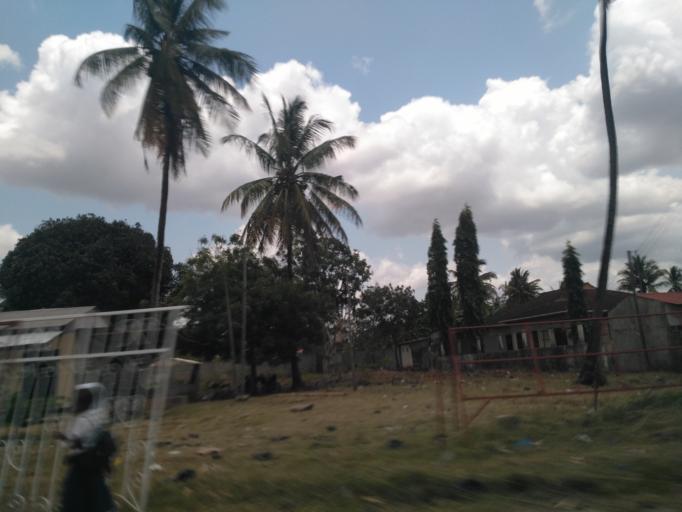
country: TZ
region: Dar es Salaam
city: Dar es Salaam
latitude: -6.8581
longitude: 39.3546
